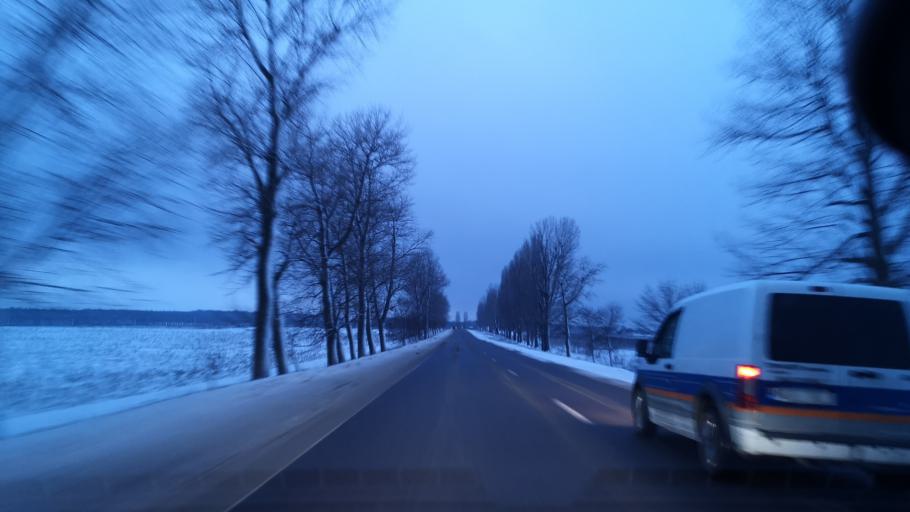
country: MD
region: Rezina
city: Rezina
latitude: 47.7375
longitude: 28.8846
